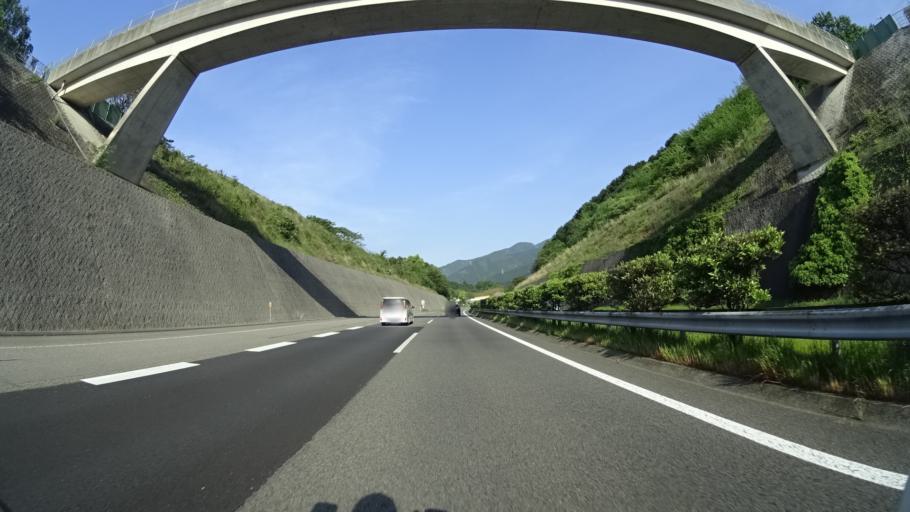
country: JP
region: Ehime
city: Saijo
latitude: 33.9121
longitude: 133.2413
